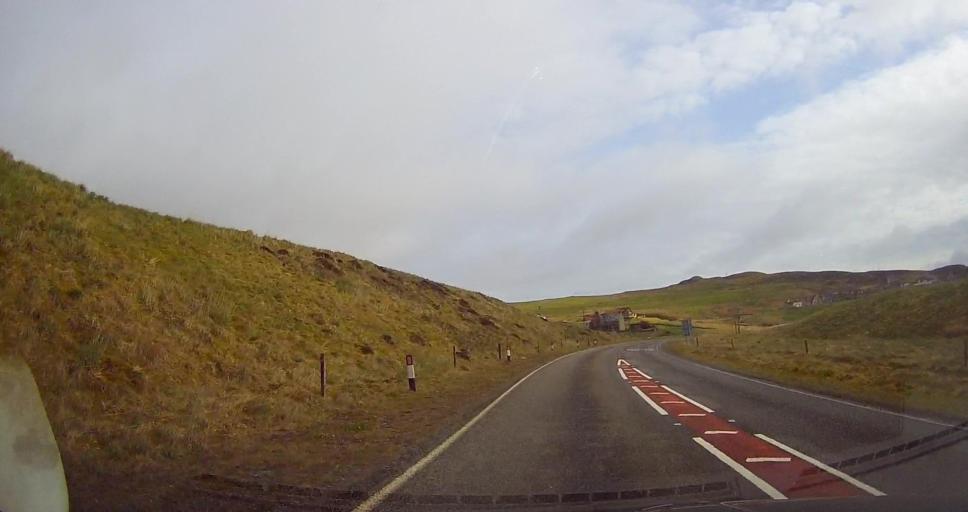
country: GB
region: Scotland
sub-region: Shetland Islands
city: Lerwick
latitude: 60.1019
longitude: -1.2340
